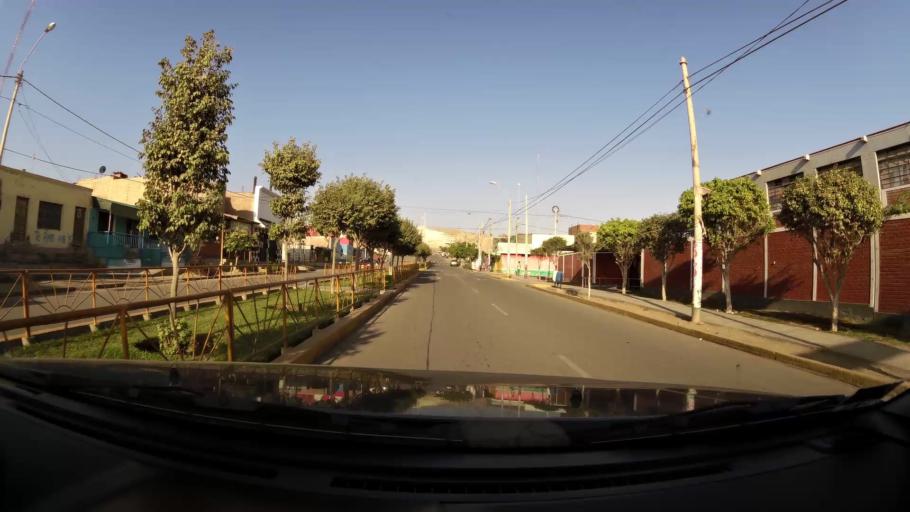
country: PE
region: Ica
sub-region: Provincia de Pisco
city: Villa Tupac Amaru
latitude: -13.7135
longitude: -76.1509
